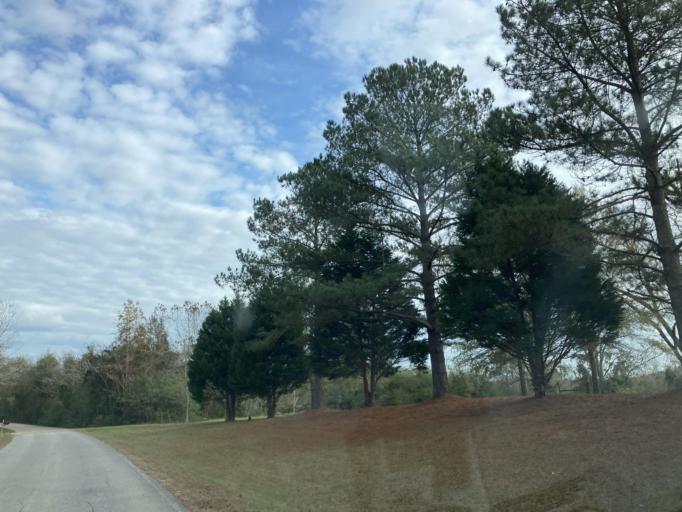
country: US
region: Mississippi
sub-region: Stone County
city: Wiggins
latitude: 30.9939
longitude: -89.2521
